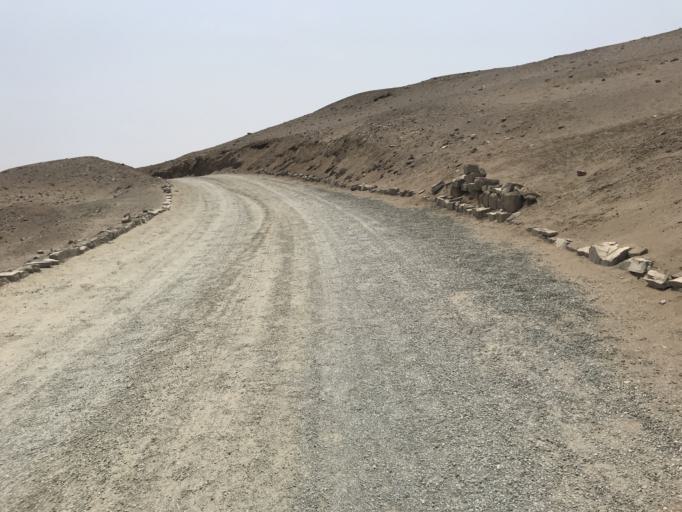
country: PE
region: Lima
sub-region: Lima
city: Punta Hermosa
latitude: -12.2554
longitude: -76.8974
